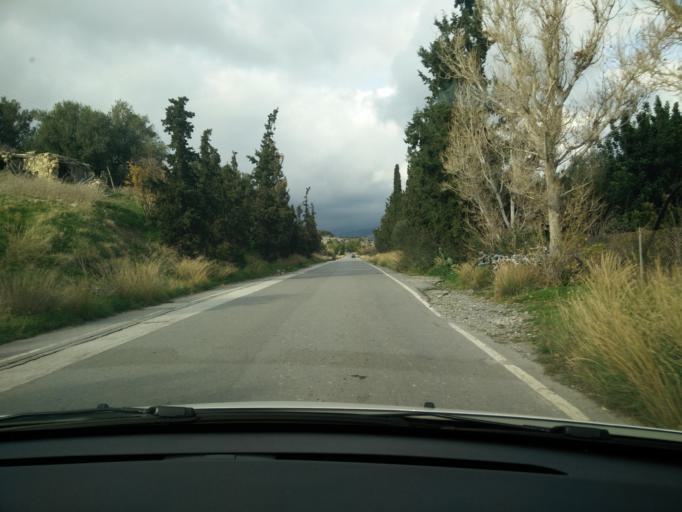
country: GR
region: Crete
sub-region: Nomos Lasithiou
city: Gra Liyia
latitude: 35.0105
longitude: 25.5836
